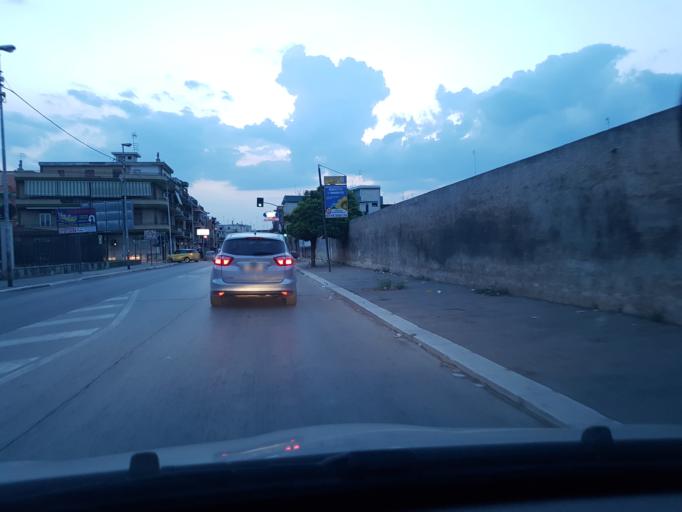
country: IT
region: Apulia
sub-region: Provincia di Foggia
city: Cerignola
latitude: 41.2597
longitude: 15.8938
